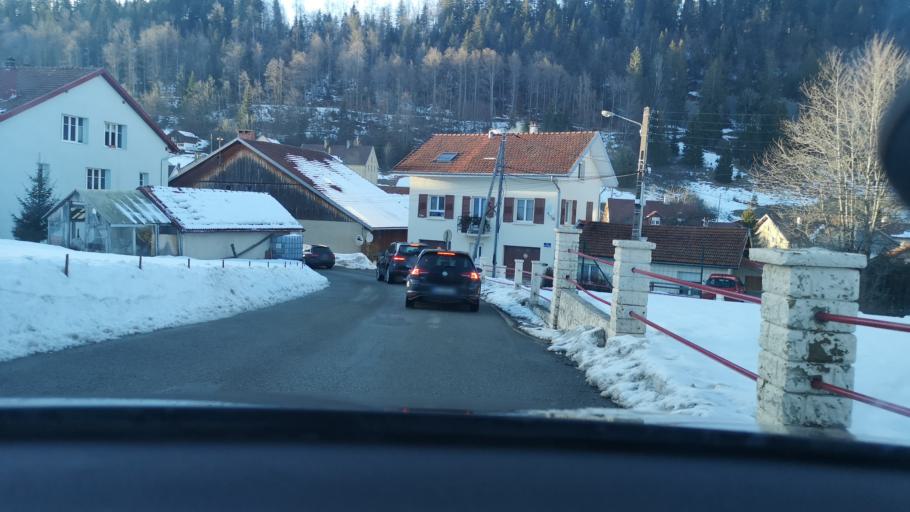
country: FR
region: Franche-Comte
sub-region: Departement du Doubs
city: Montlebon
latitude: 46.9946
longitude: 6.5461
